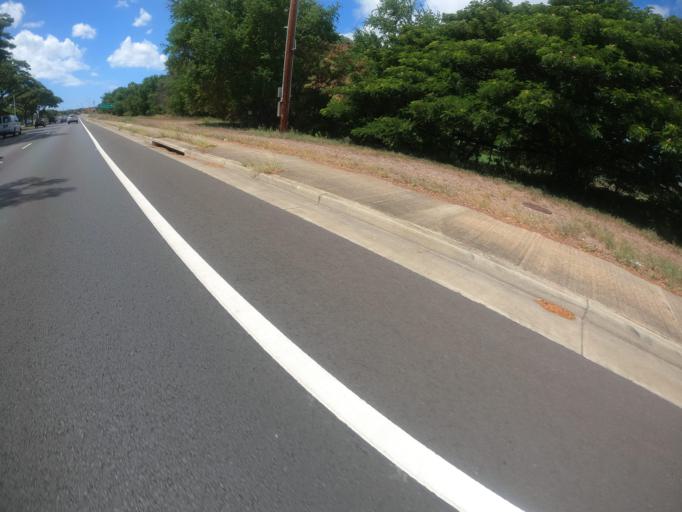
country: US
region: Hawaii
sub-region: Honolulu County
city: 'Ewa Gentry
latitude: 21.3632
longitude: -158.0278
